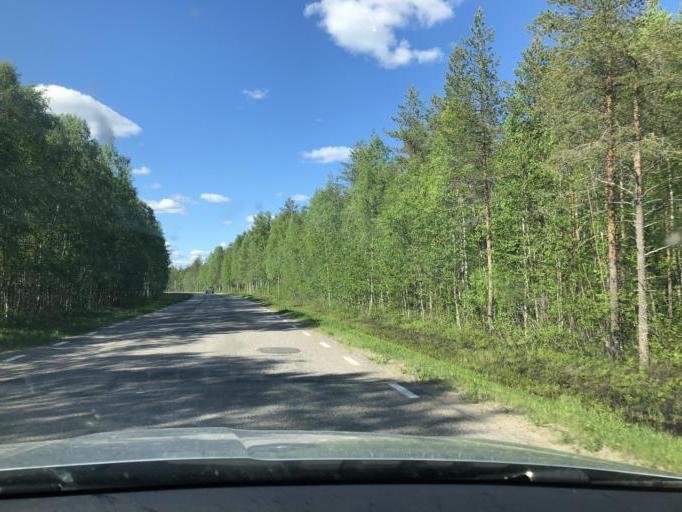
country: SE
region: Norrbotten
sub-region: Kalix Kommun
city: Kalix
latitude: 65.9172
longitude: 23.1729
